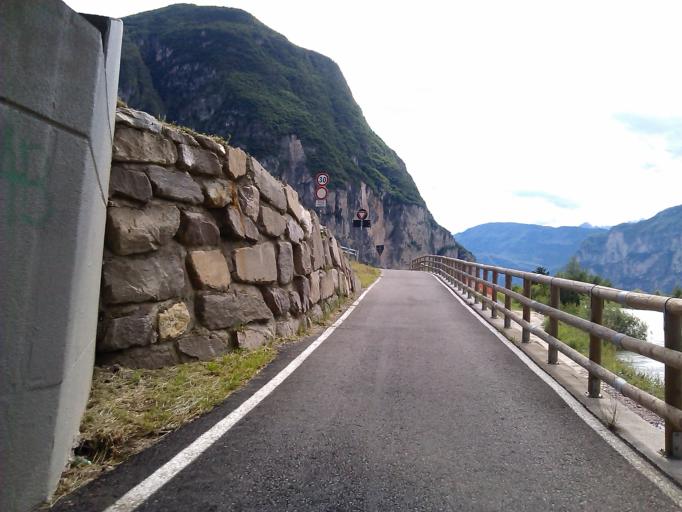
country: IT
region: Trentino-Alto Adige
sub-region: Bolzano
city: Salorno
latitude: 46.2439
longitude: 11.2052
